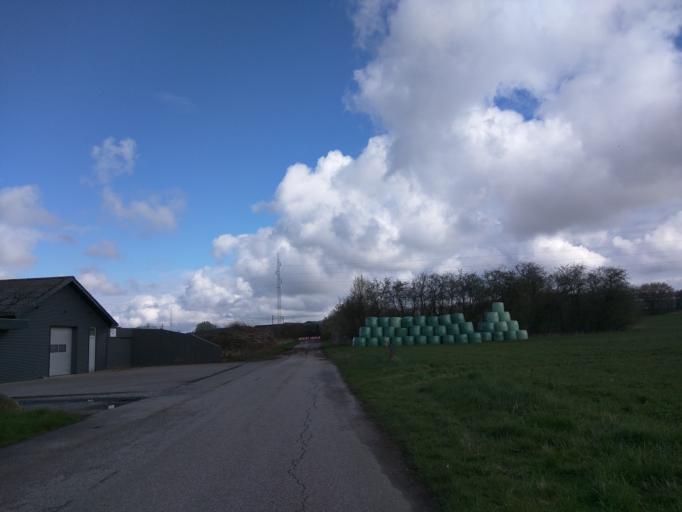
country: DK
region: South Denmark
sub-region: Fredericia Kommune
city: Snoghoj
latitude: 55.5402
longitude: 9.6921
